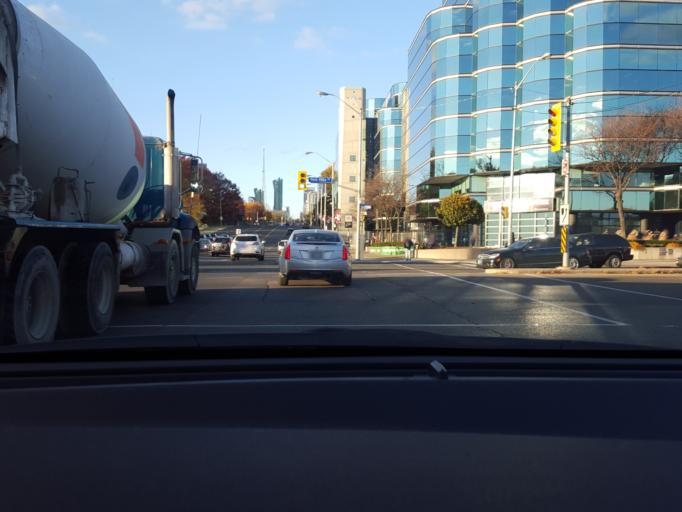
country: CA
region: Ontario
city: Willowdale
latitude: 43.7440
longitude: -79.4065
